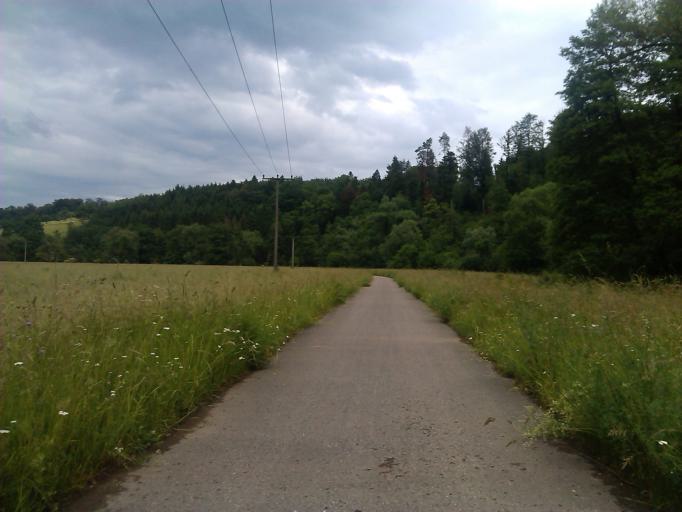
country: DE
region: Baden-Wuerttemberg
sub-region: Regierungsbezirk Stuttgart
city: Obergroningen
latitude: 48.9070
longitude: 9.9345
